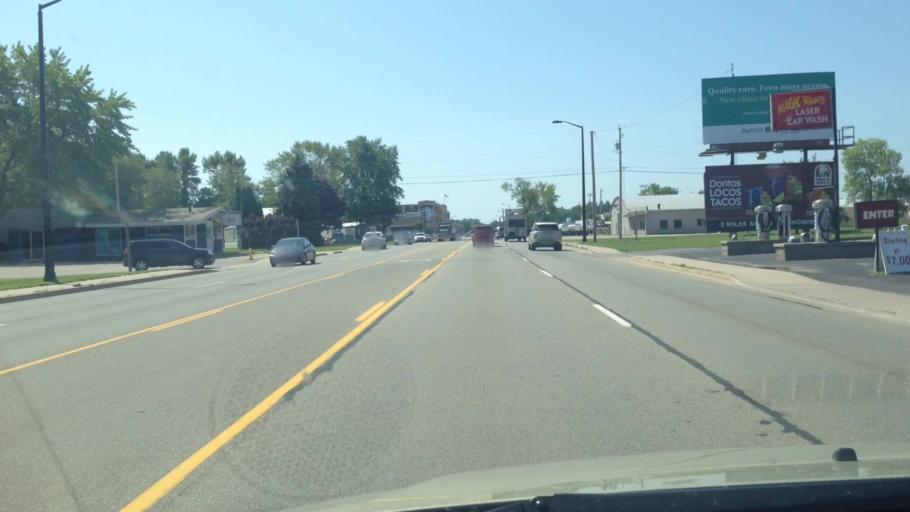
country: US
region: Michigan
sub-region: Menominee County
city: Menominee
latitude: 45.1304
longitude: -87.6128
